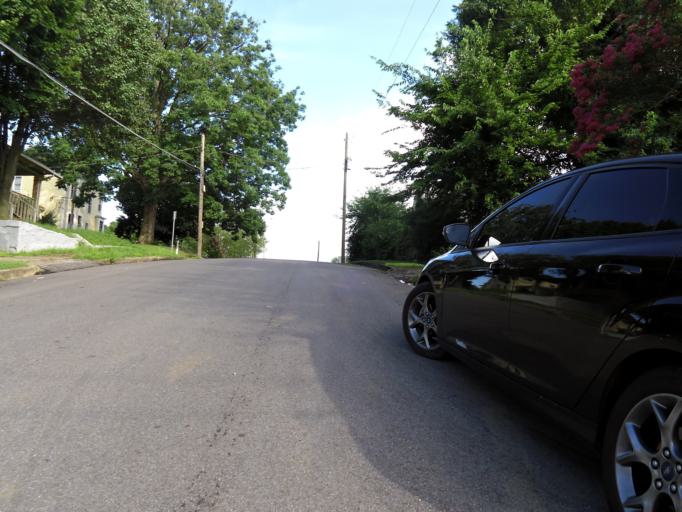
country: US
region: Tennessee
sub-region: Knox County
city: Knoxville
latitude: 35.9859
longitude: -83.9294
